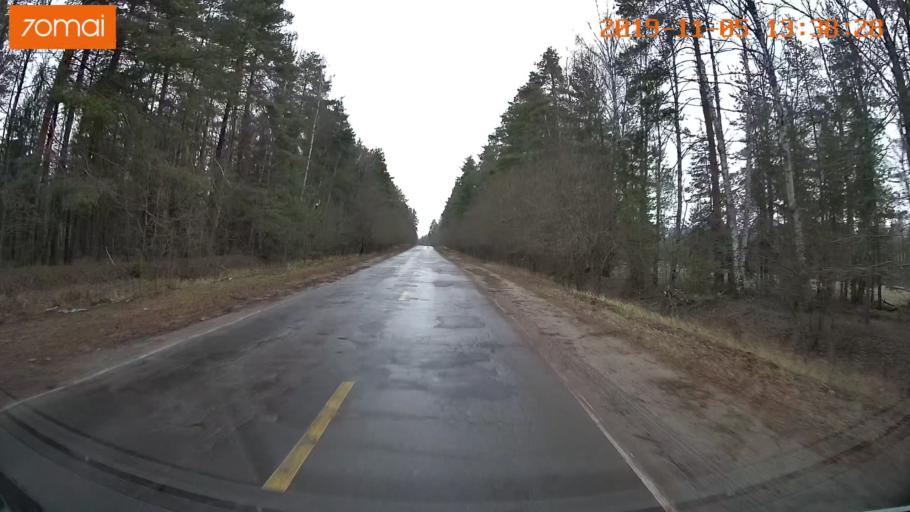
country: RU
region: Ivanovo
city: Shuya
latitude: 56.9321
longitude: 41.3867
